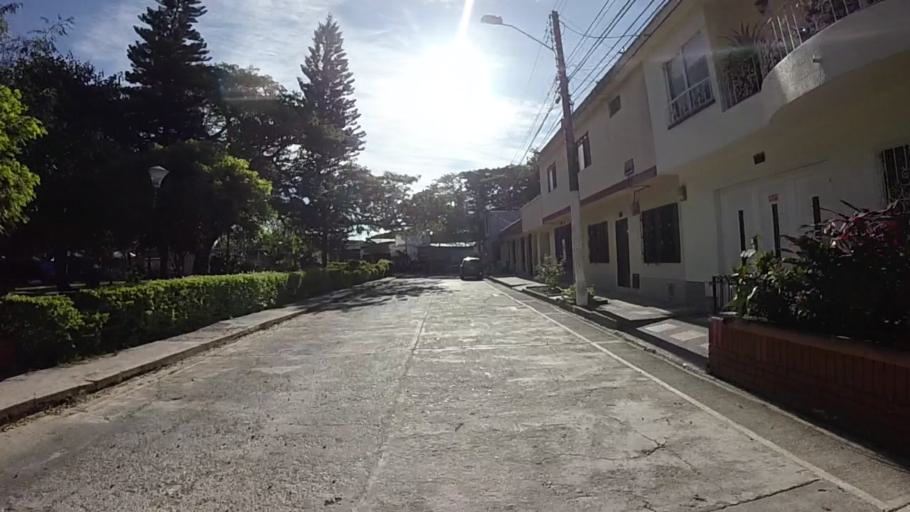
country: CO
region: Valle del Cauca
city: Cartago
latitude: 4.7524
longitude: -75.9225
